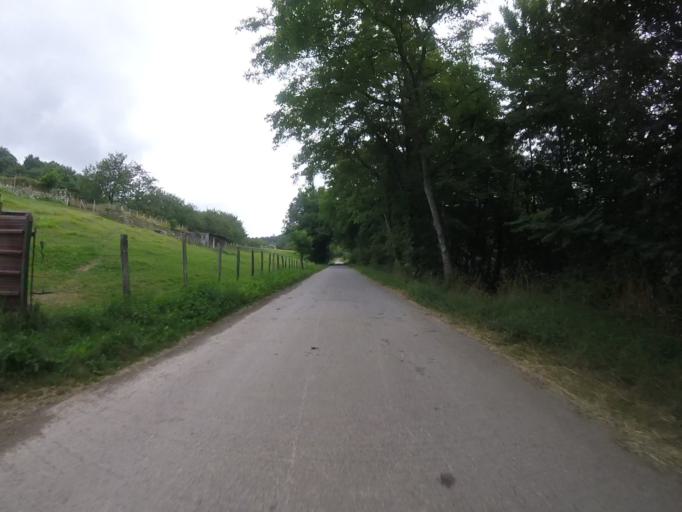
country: ES
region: Navarre
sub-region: Provincia de Navarra
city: Sunbilla
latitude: 43.1613
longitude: -1.6714
